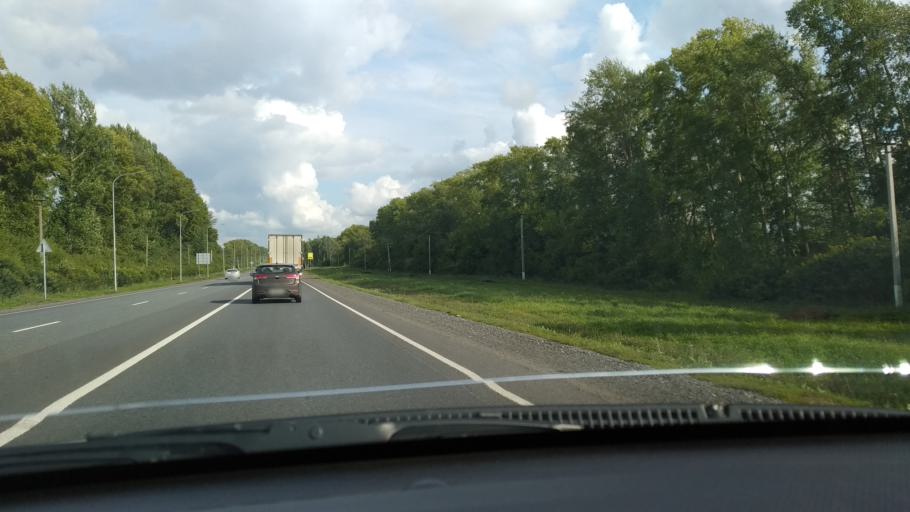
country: RU
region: Tatarstan
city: Stolbishchi
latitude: 55.6544
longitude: 49.3155
